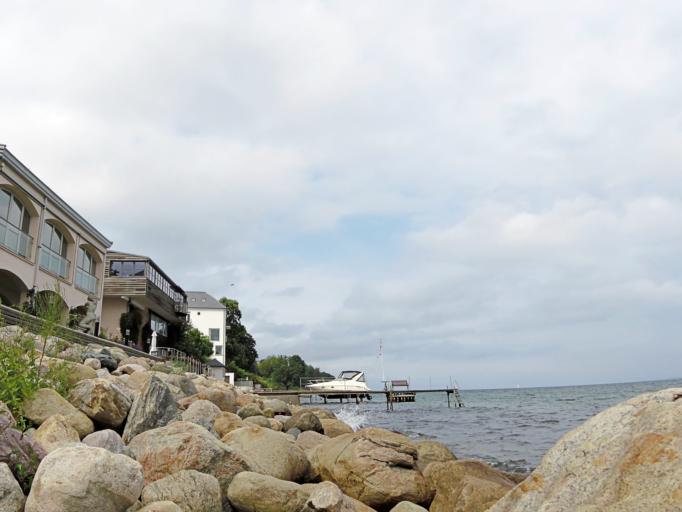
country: DK
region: Capital Region
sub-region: Gentofte Kommune
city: Charlottenlund
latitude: 55.7937
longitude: 12.5915
